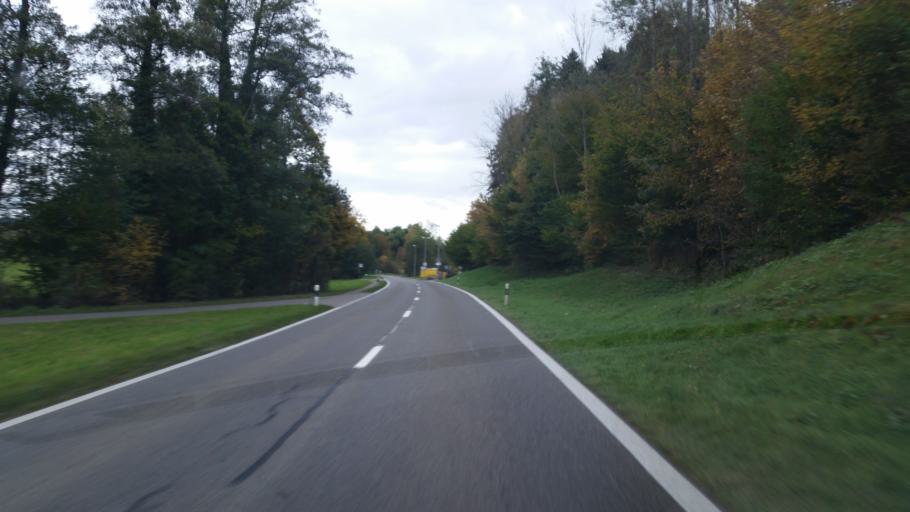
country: CH
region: Aargau
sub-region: Bezirk Zurzach
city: Oberendingen
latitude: 47.5337
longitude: 8.2948
